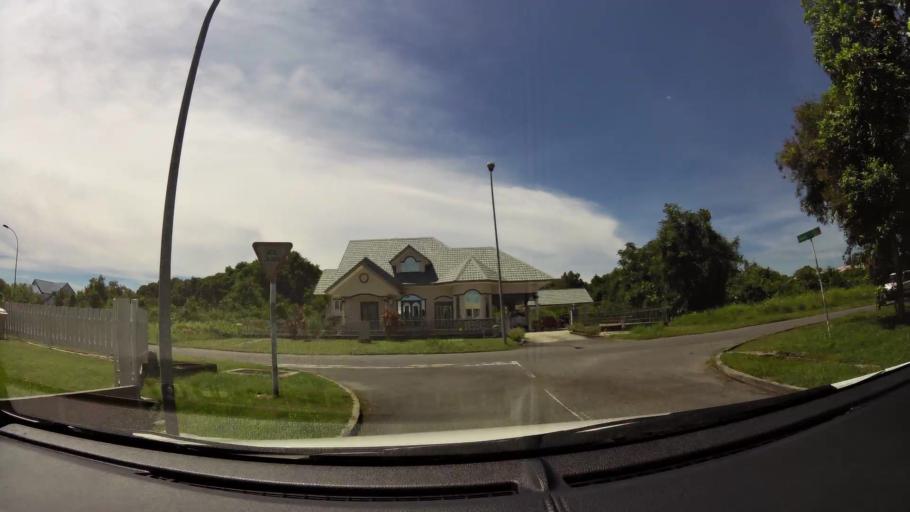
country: BN
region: Belait
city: Kuala Belait
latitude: 4.5887
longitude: 114.2263
